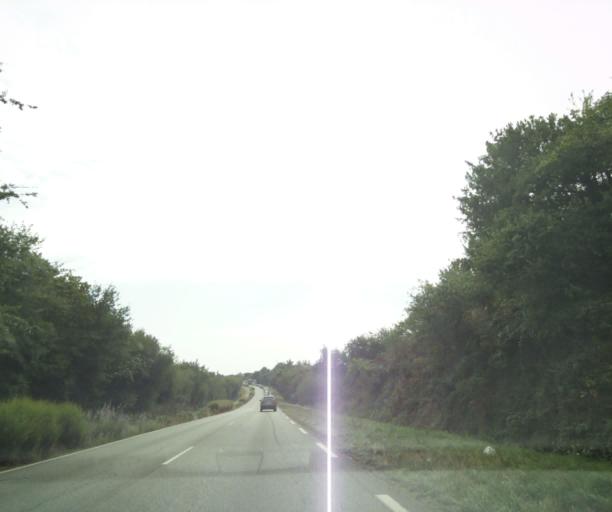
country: FR
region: Pays de la Loire
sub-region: Departement de la Loire-Atlantique
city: Saint-Herblain
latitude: 47.2127
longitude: -1.6336
